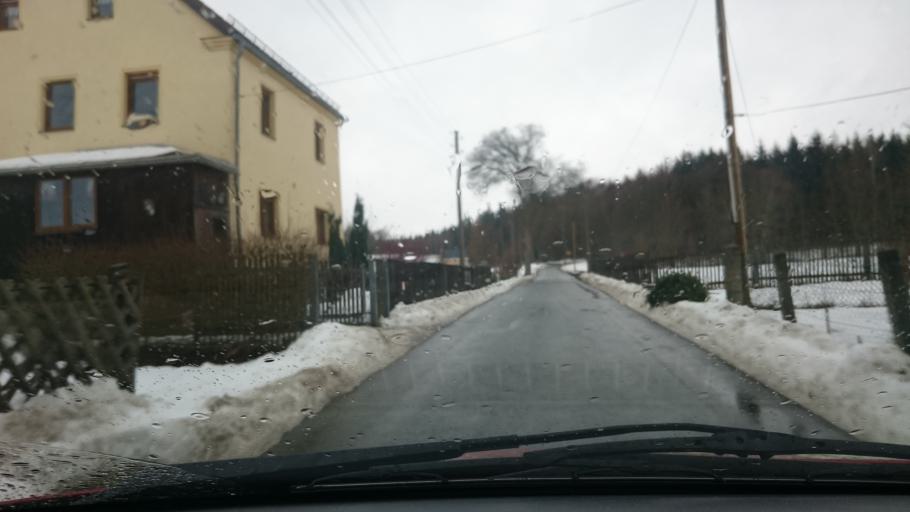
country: DE
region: Saxony
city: Markneukirchen
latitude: 50.2993
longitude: 12.2958
